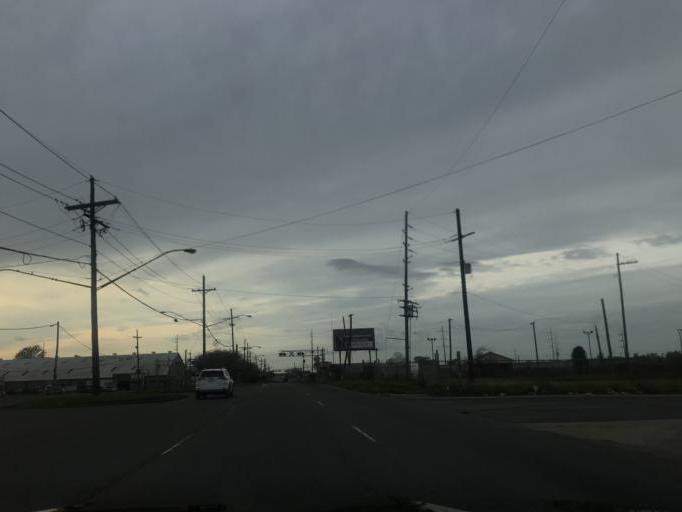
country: US
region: Louisiana
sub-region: Jefferson Parish
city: Jefferson
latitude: 29.9649
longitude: -90.1332
